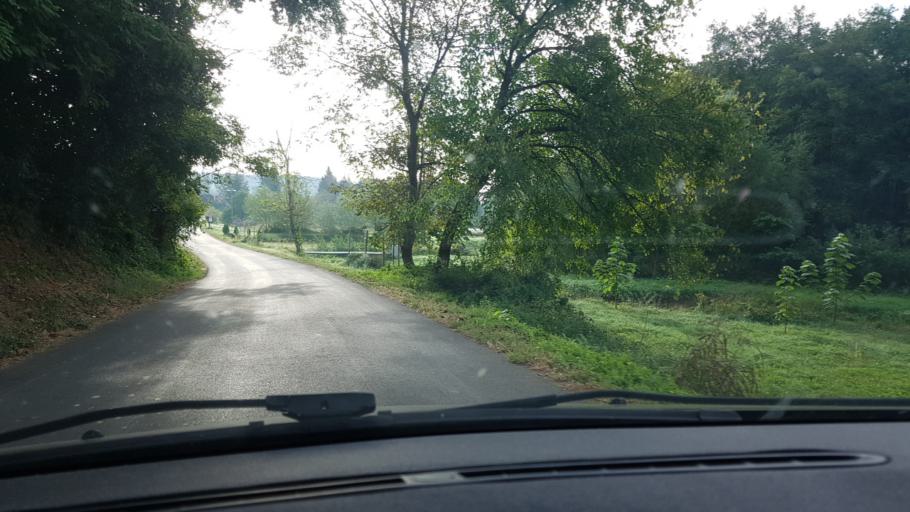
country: HR
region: Krapinsko-Zagorska
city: Zlatar
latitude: 46.1006
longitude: 16.1284
